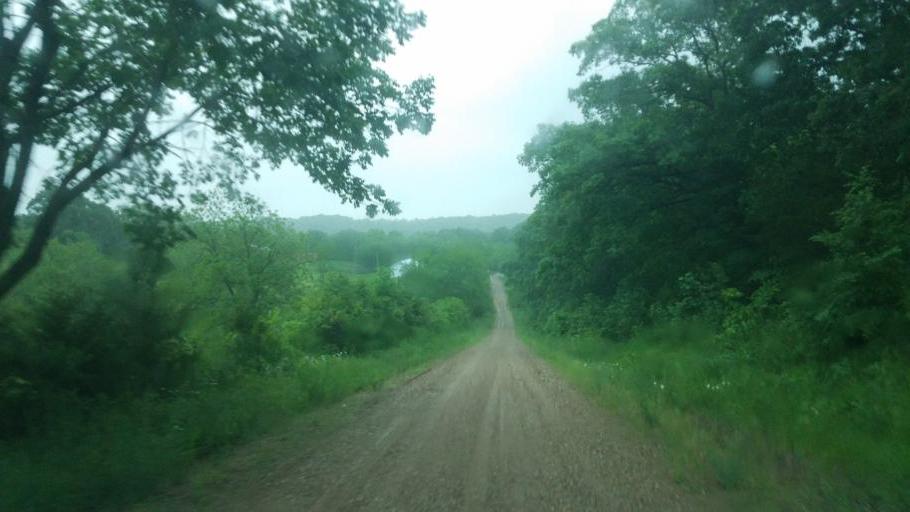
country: US
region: Missouri
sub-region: Moniteau County
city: California
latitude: 38.7247
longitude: -92.6277
